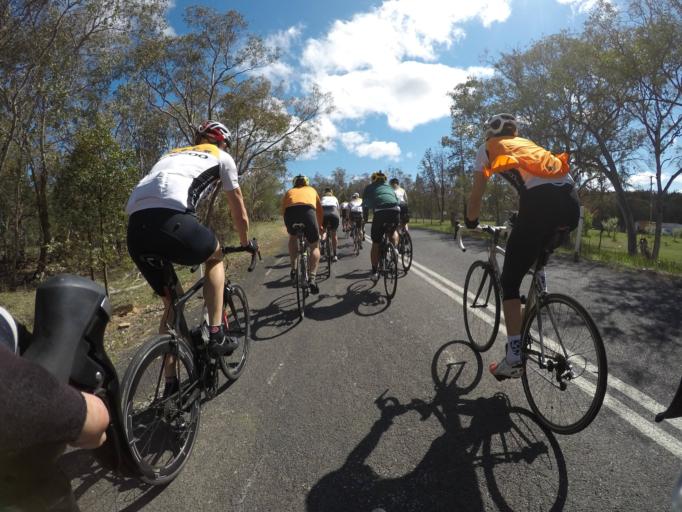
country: AU
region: New South Wales
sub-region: Parkes
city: Peak Hill
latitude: -32.6476
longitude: 148.5512
